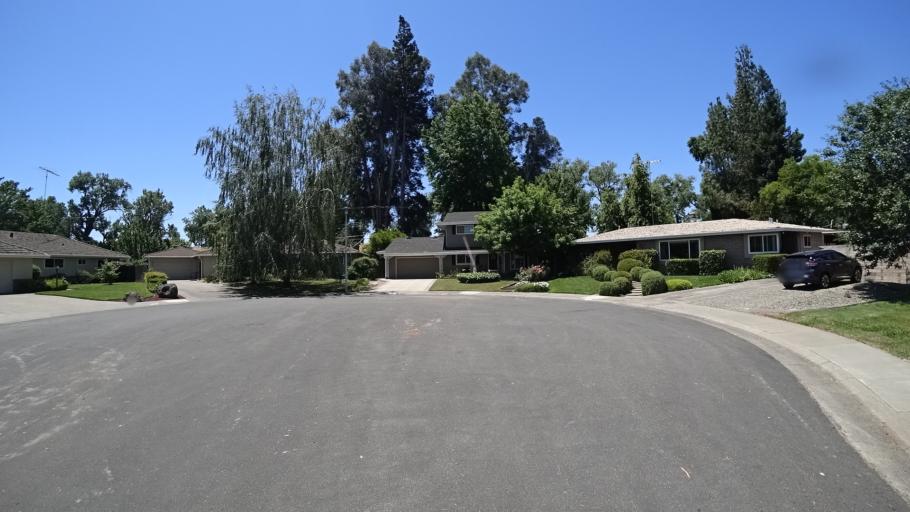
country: US
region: California
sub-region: Yolo County
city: West Sacramento
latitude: 38.5263
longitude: -121.5265
